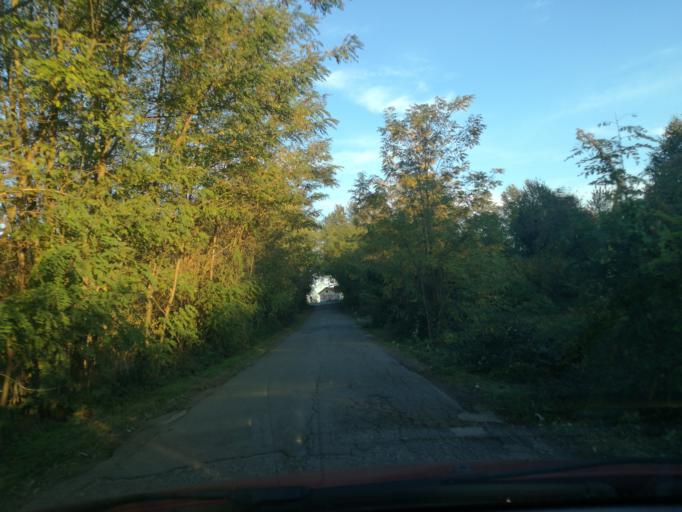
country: IT
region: Lombardy
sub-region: Provincia di Monza e Brianza
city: Ornago
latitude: 45.6043
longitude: 9.4049
